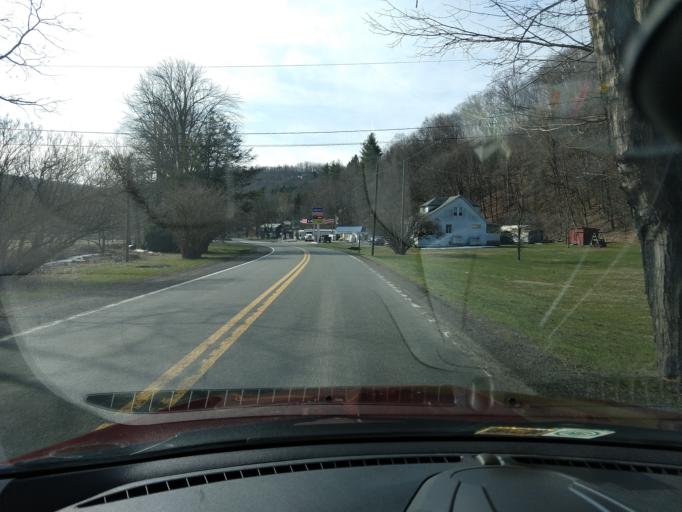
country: US
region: West Virginia
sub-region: Pocahontas County
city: Marlinton
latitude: 38.1882
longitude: -80.1352
